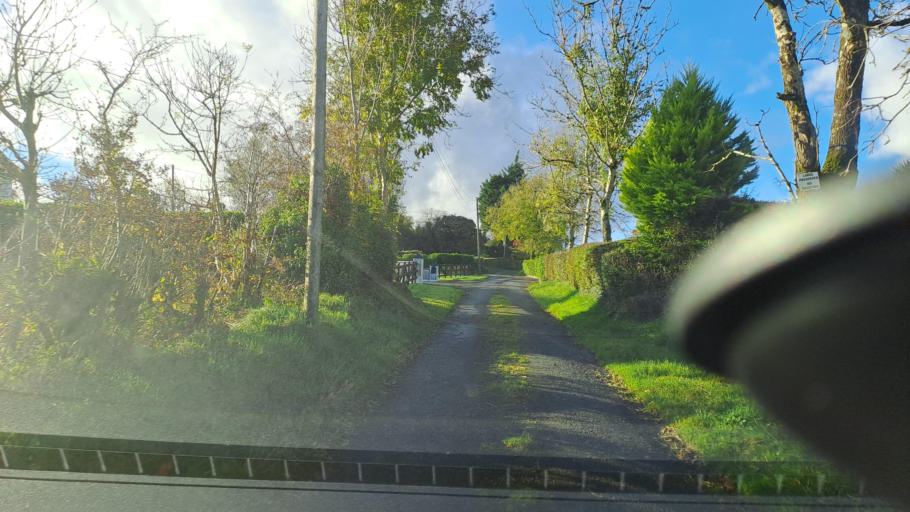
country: IE
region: Ulster
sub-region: An Cabhan
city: Bailieborough
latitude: 53.9344
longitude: -6.9467
